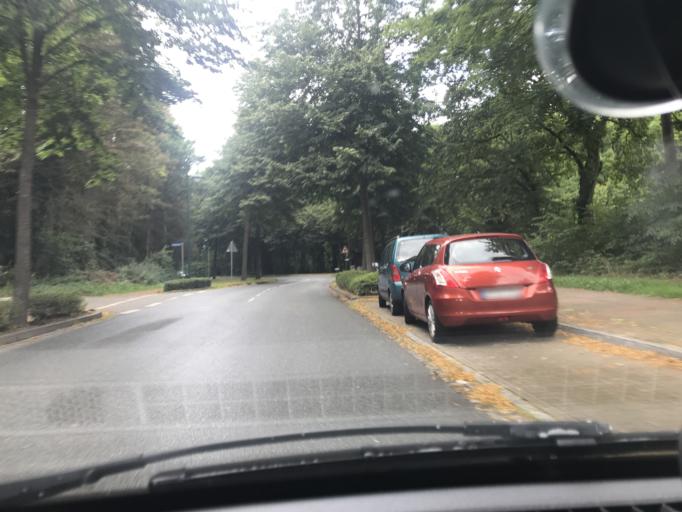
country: DE
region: Schleswig-Holstein
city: Grosshansdorf
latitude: 53.6564
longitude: 10.2605
